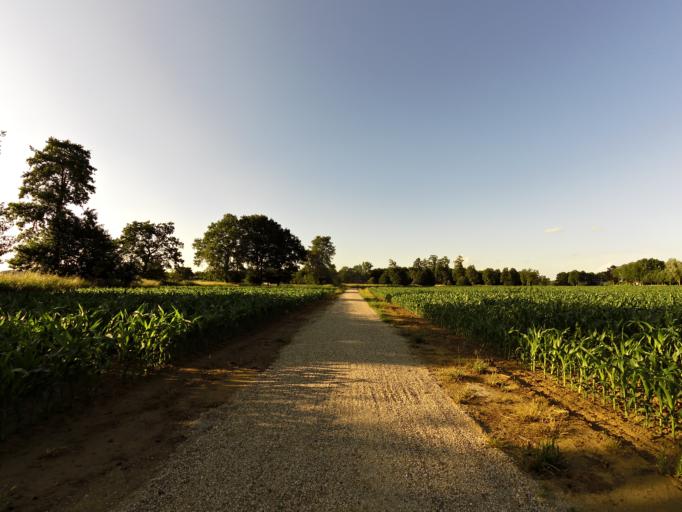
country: NL
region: Gelderland
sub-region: Oude IJsselstreek
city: Wisch
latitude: 51.8859
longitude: 6.4186
